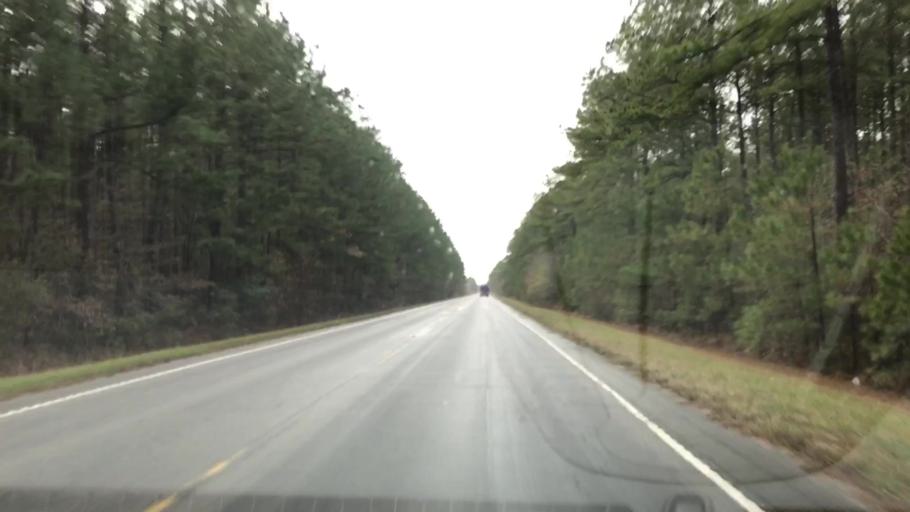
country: US
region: South Carolina
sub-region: Berkeley County
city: Saint Stephen
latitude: 33.2869
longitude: -79.8474
